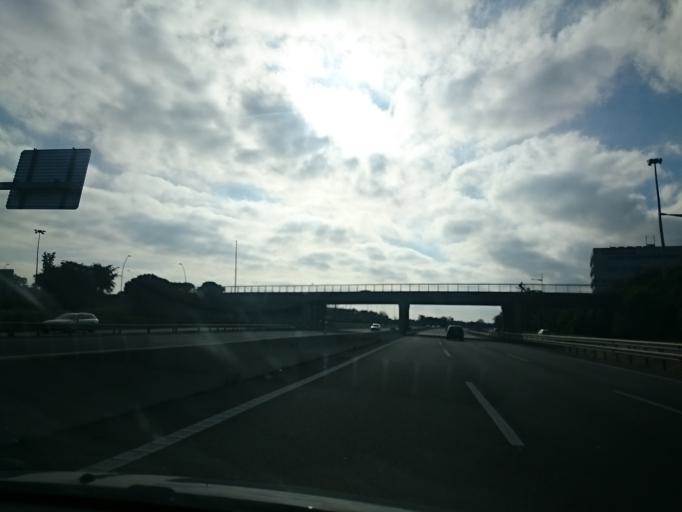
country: ES
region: Catalonia
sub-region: Provincia de Barcelona
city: Castelldefels
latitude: 41.2801
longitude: 1.9898
